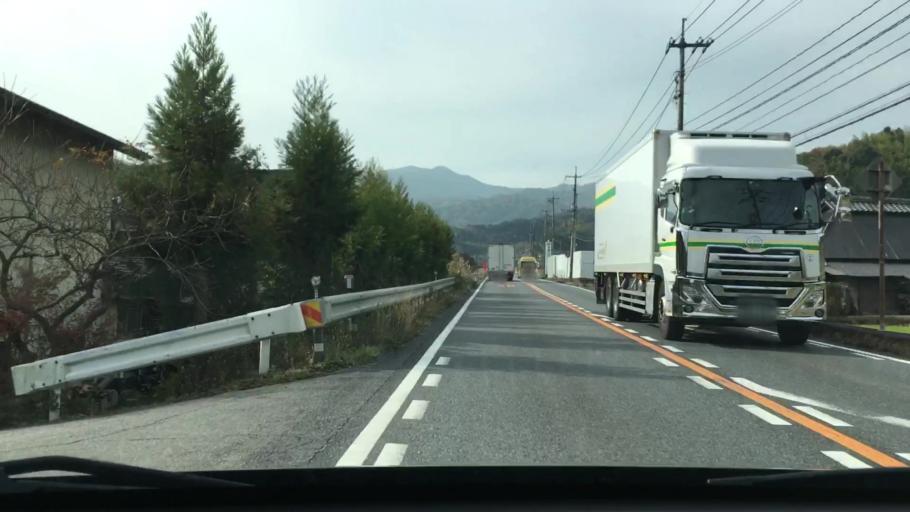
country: JP
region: Yamaguchi
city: Hikari
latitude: 34.0932
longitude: 132.0230
